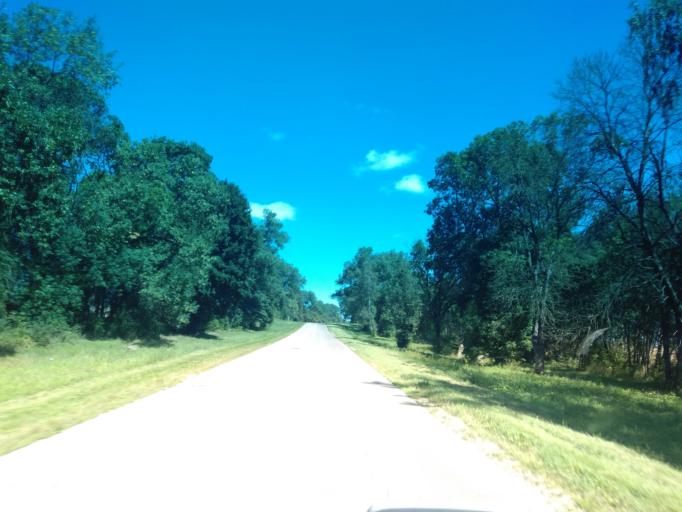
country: BY
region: Minsk
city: Stan'kava
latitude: 53.6415
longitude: 27.2913
